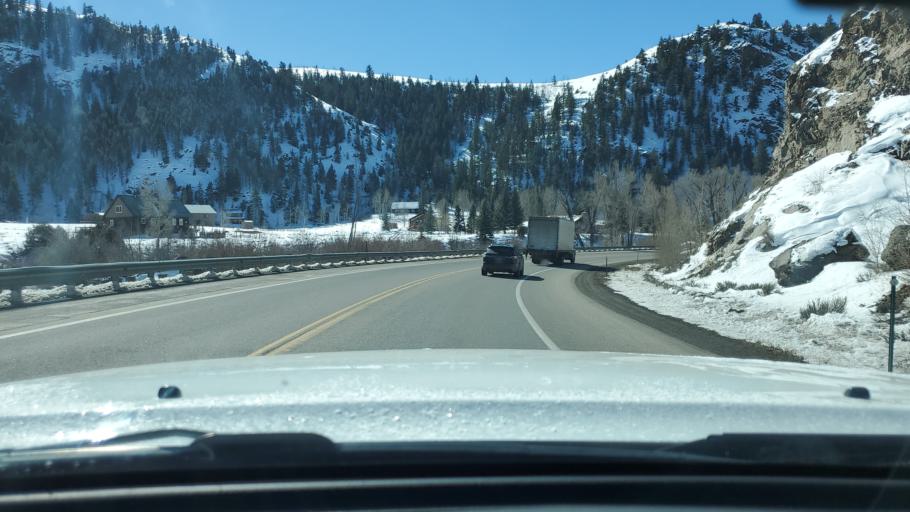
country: US
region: Colorado
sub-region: Gunnison County
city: Gunnison
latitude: 38.6624
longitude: -106.8480
